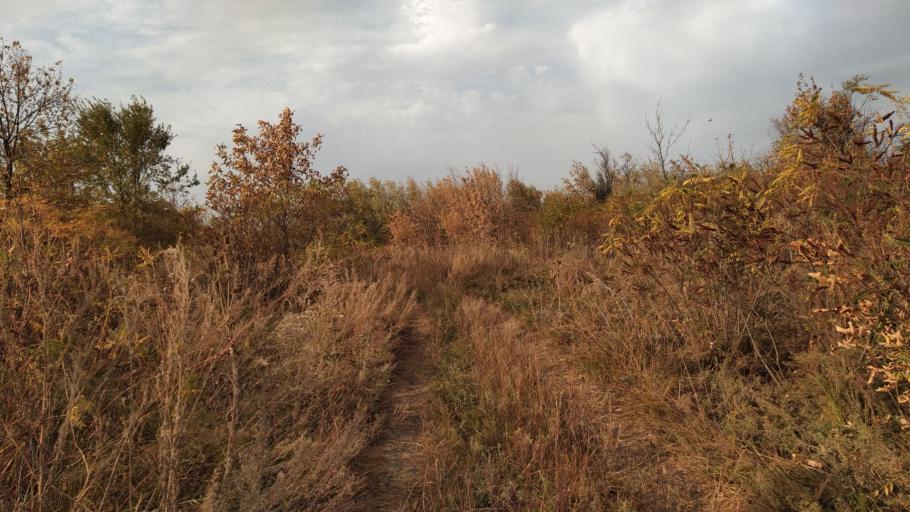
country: RU
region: Rostov
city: Kuleshovka
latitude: 47.1430
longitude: 39.5850
